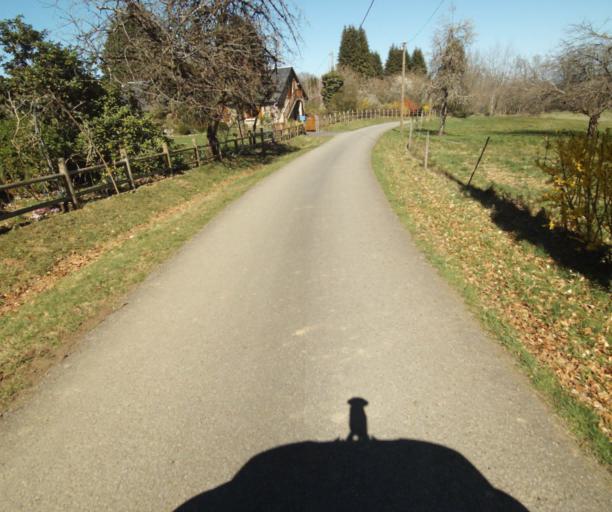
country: FR
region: Limousin
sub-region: Departement de la Correze
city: Uzerche
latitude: 45.3891
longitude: 1.6065
